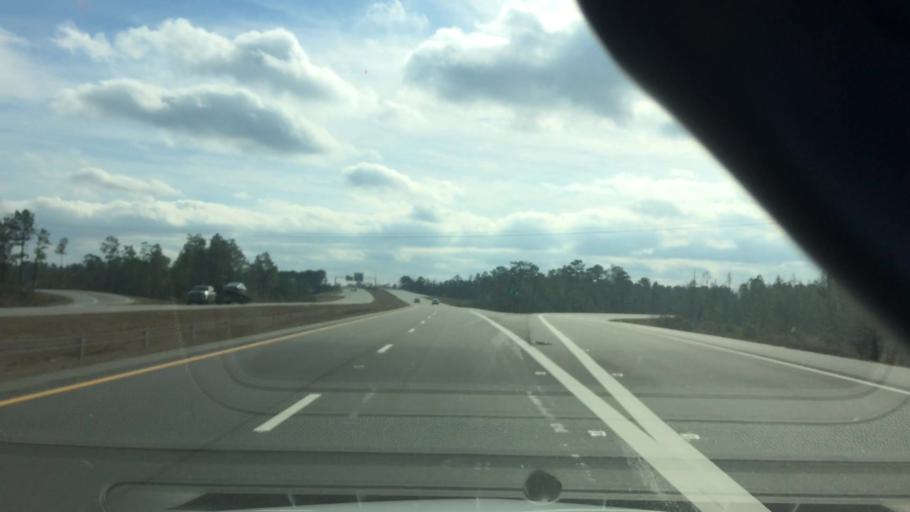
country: US
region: North Carolina
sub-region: Brunswick County
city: Leland
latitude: 34.2638
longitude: -78.0798
